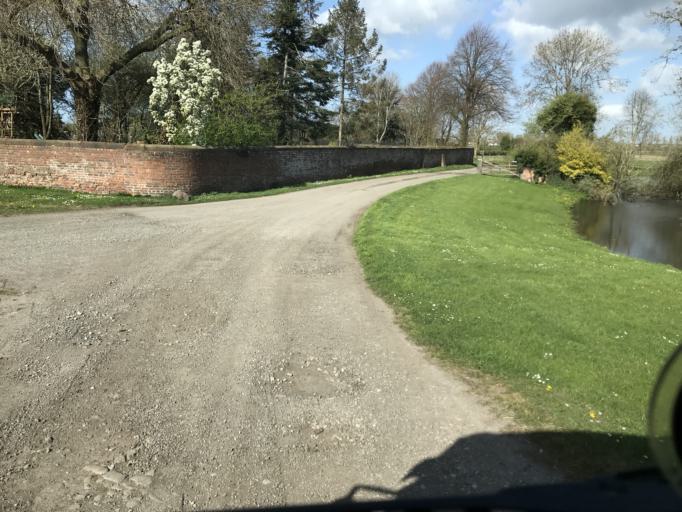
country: GB
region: England
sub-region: Cheshire West and Chester
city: Blacon
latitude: 53.1667
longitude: -2.9505
